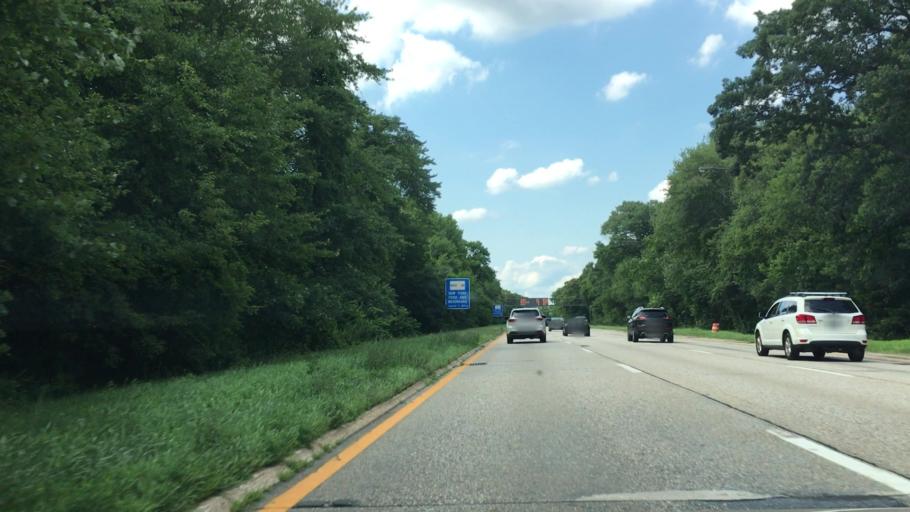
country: US
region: New York
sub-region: Nassau County
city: North Merrick
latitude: 40.6728
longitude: -73.5701
